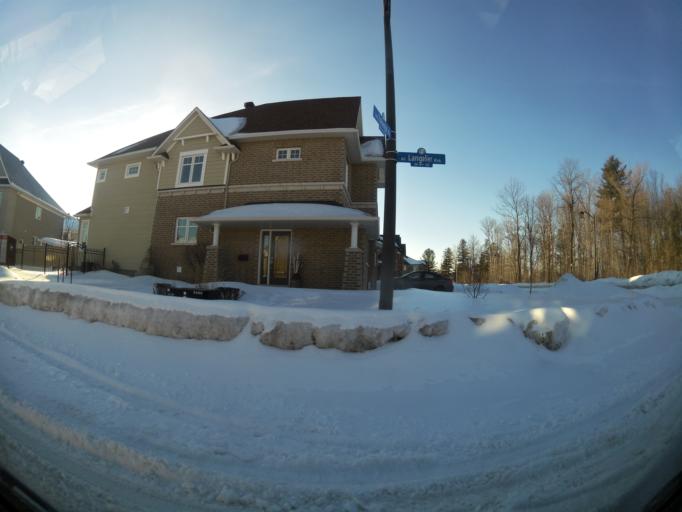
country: CA
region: Ontario
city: Ottawa
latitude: 45.4339
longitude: -75.5159
